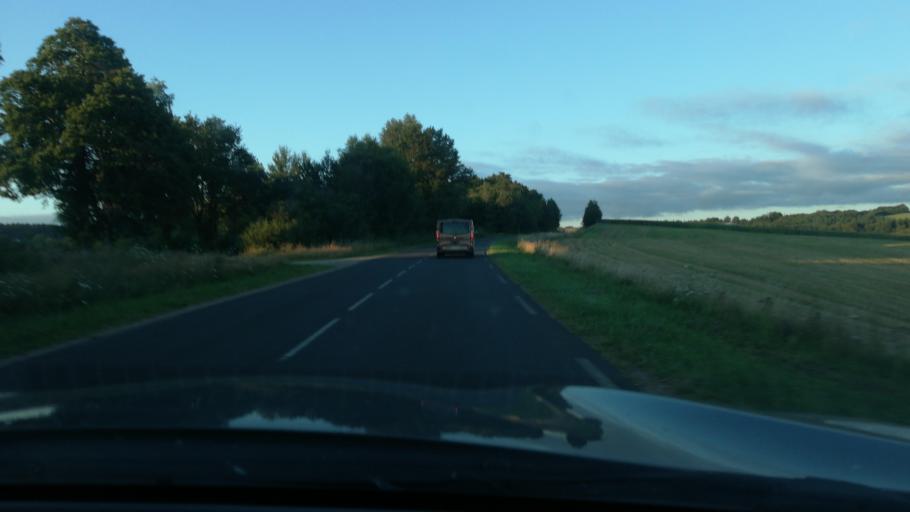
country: FR
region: Auvergne
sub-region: Departement du Cantal
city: Laroquebrou
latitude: 44.9425
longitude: 2.0863
